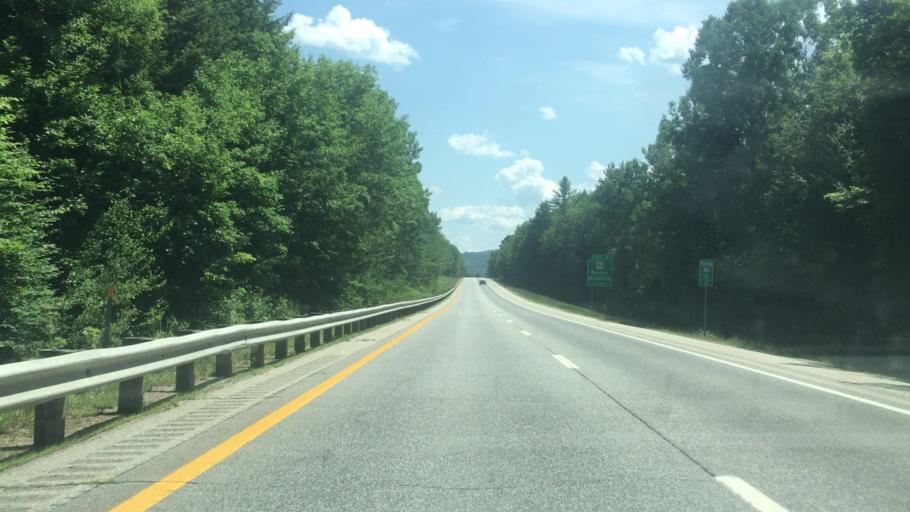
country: US
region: New Hampshire
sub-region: Merrimack County
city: Sutton
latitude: 43.3059
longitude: -71.8439
